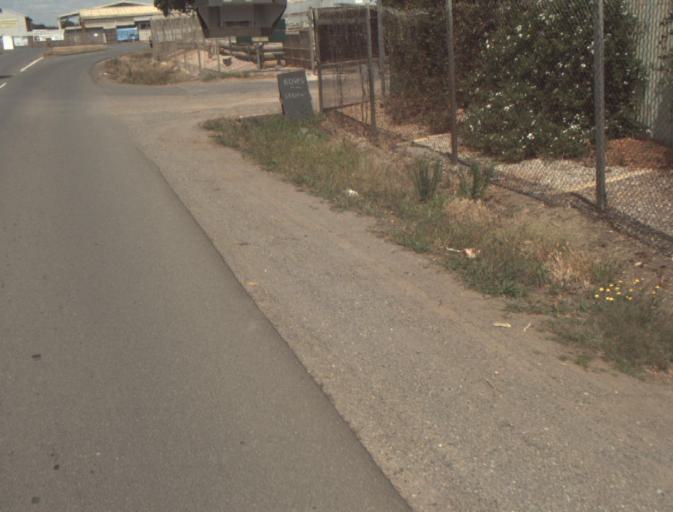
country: AU
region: Tasmania
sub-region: Launceston
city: Newnham
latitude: -41.4032
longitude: 147.1482
